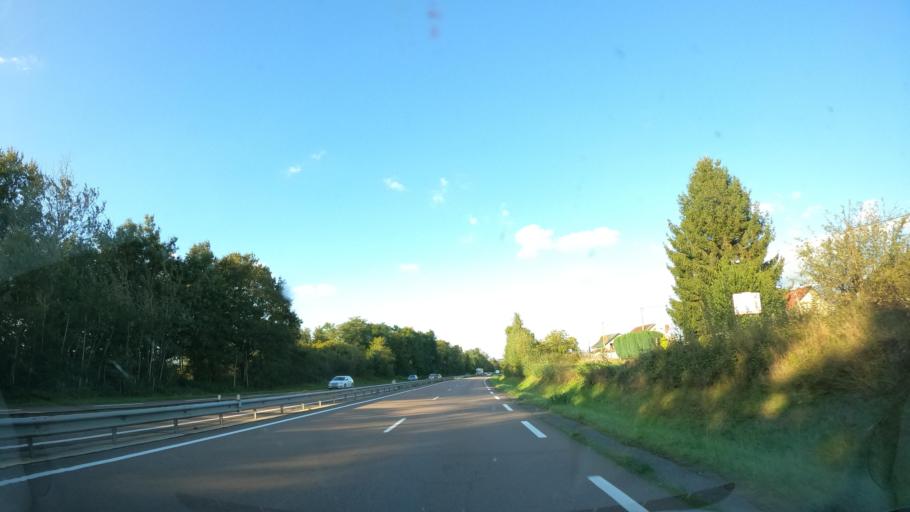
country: FR
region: Bourgogne
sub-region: Departement de Saone-et-Loire
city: Montceau-les-Mines
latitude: 46.6580
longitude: 4.3310
